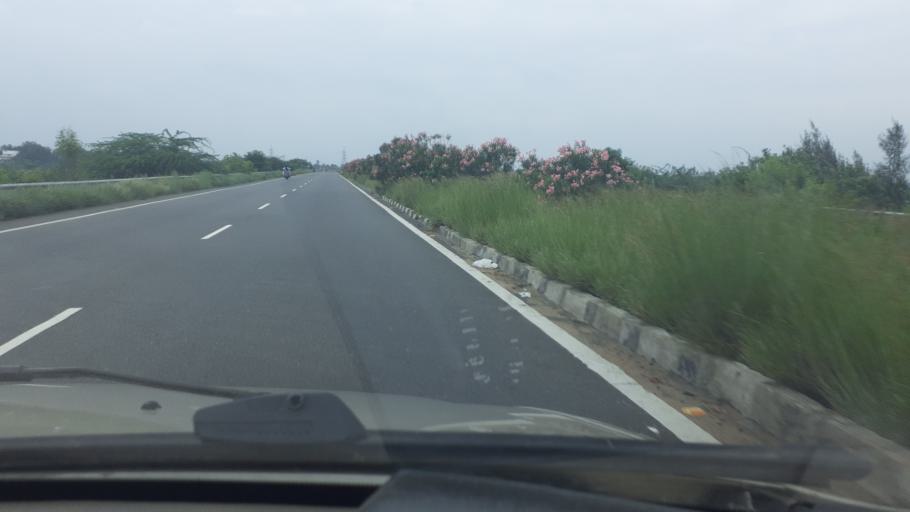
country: IN
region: Tamil Nadu
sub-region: Madurai
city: Tirupparangunram
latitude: 9.8359
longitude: 77.9952
